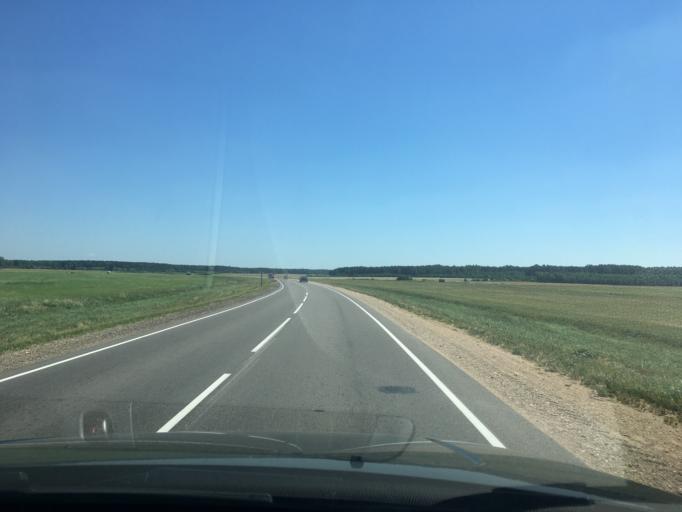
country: BY
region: Grodnenskaya
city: Iwye
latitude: 53.9124
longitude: 25.7745
